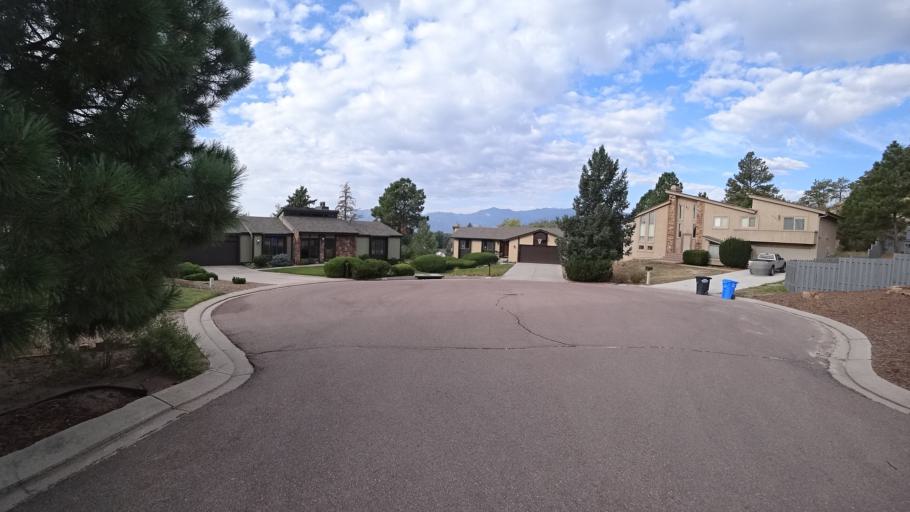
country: US
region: Colorado
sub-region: El Paso County
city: Cimarron Hills
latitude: 38.8671
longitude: -104.7499
